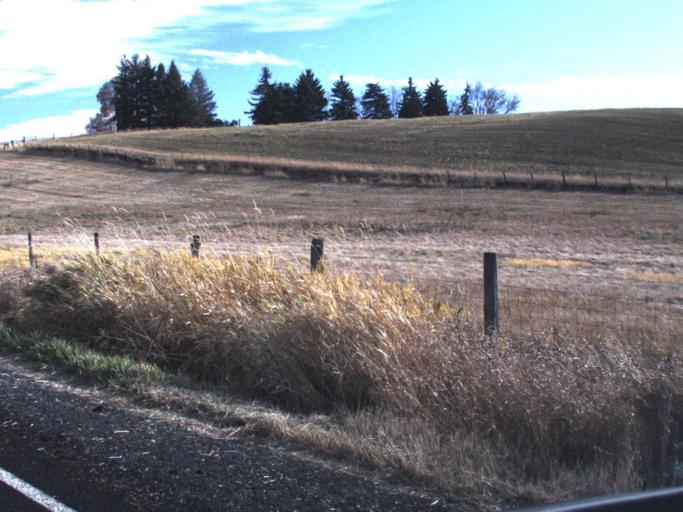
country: US
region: Washington
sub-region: Whitman County
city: Colfax
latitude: 46.9346
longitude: -117.2118
